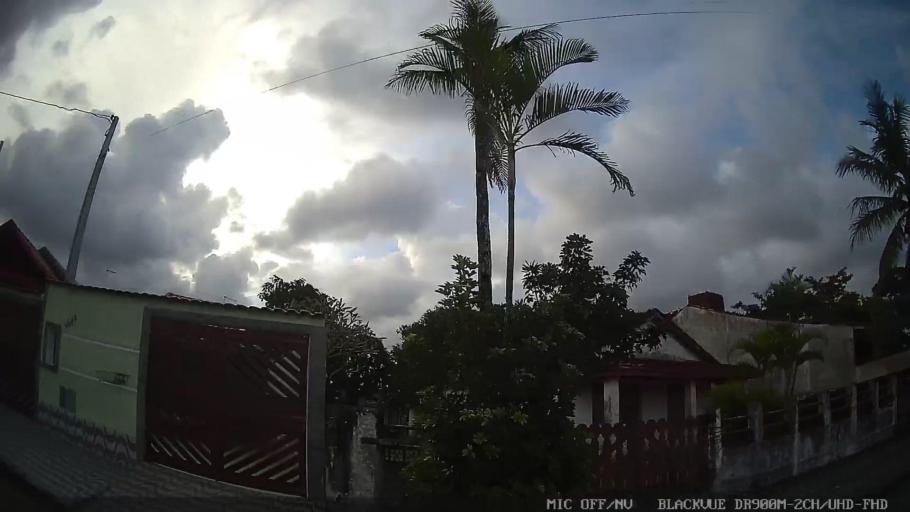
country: BR
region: Sao Paulo
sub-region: Mongagua
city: Mongagua
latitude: -24.1217
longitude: -46.6781
